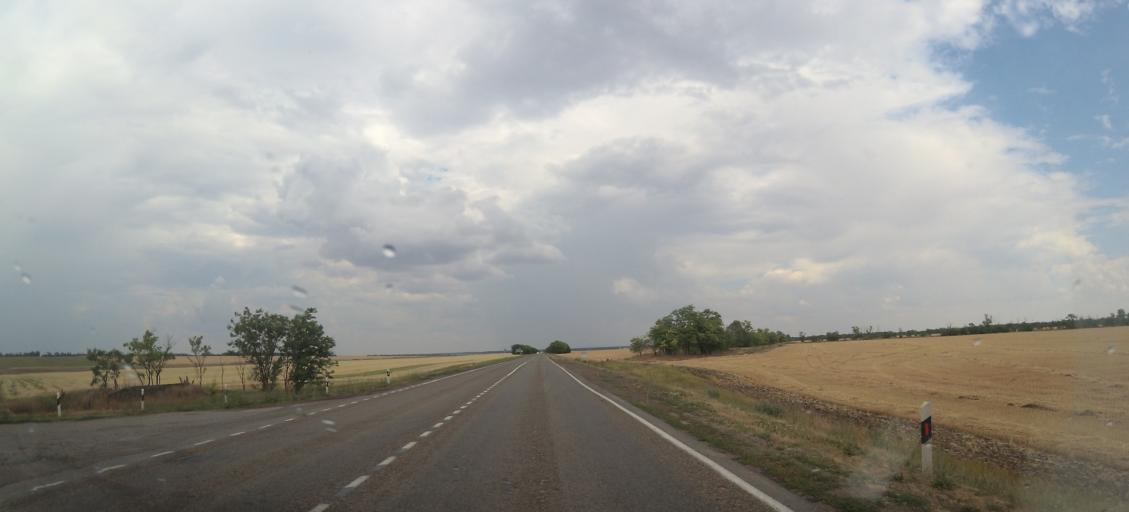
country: RU
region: Rostov
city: Gigant
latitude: 46.3329
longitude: 41.3895
